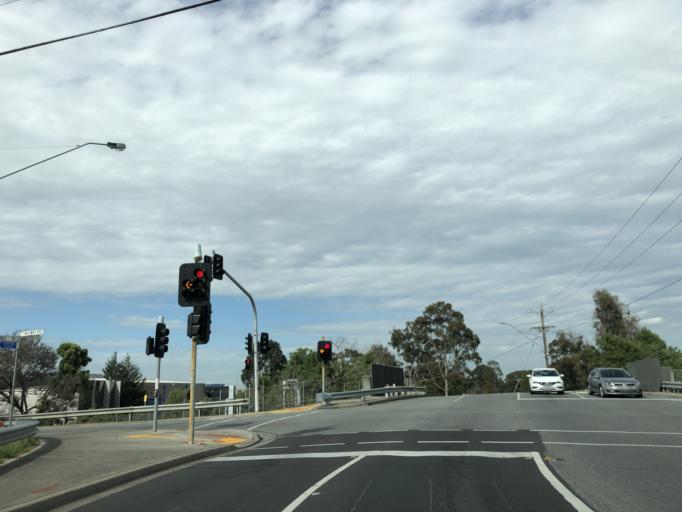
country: AU
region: Victoria
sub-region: Greater Dandenong
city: Dandenong
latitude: -37.9838
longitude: 145.2005
